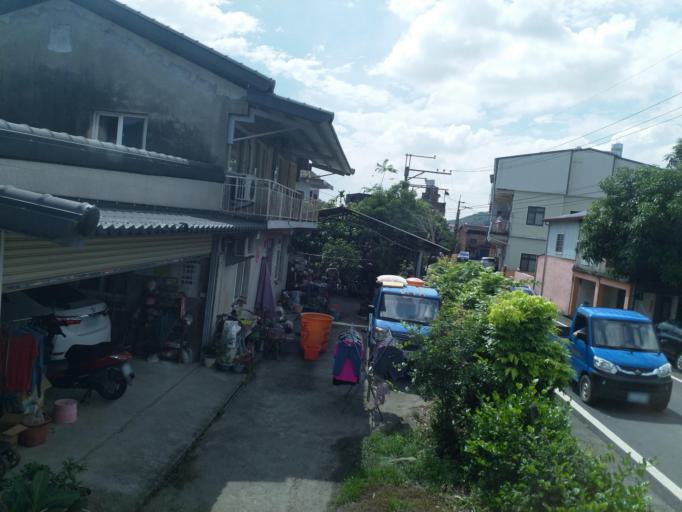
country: TW
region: Taiwan
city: Yujing
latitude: 22.9220
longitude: 120.5799
